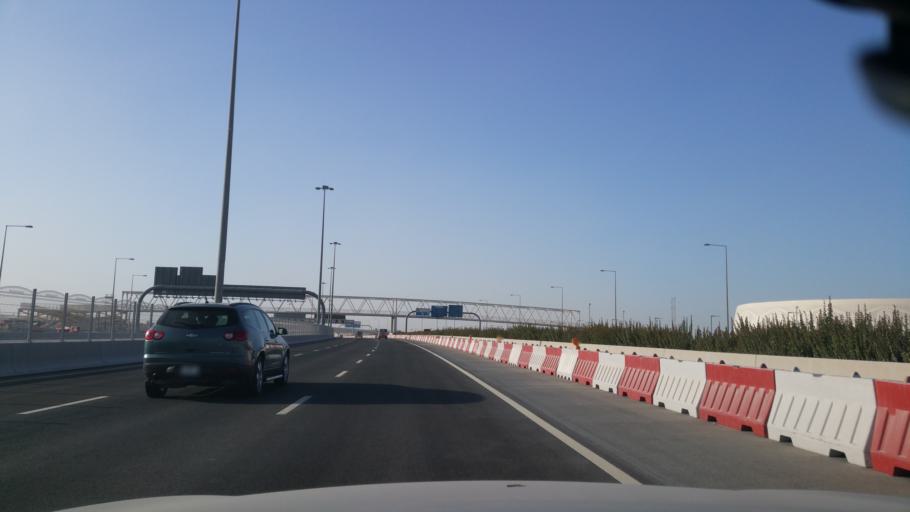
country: QA
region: Baladiyat ad Dawhah
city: Doha
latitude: 25.2292
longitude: 51.5316
